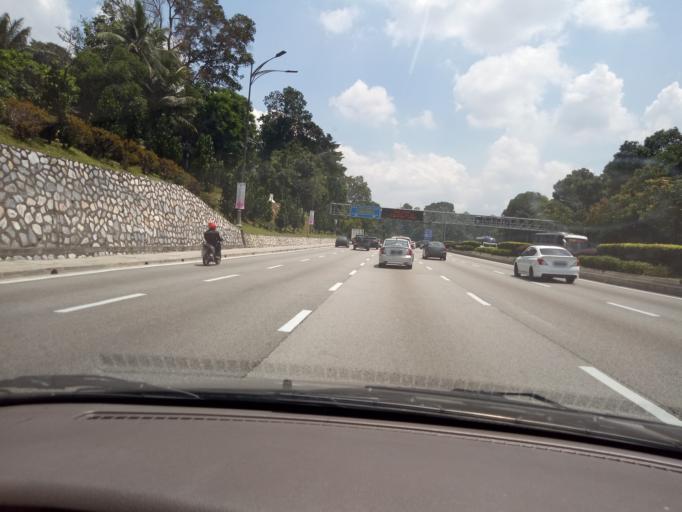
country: MY
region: Kuala Lumpur
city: Kuala Lumpur
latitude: 3.1406
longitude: 101.6803
